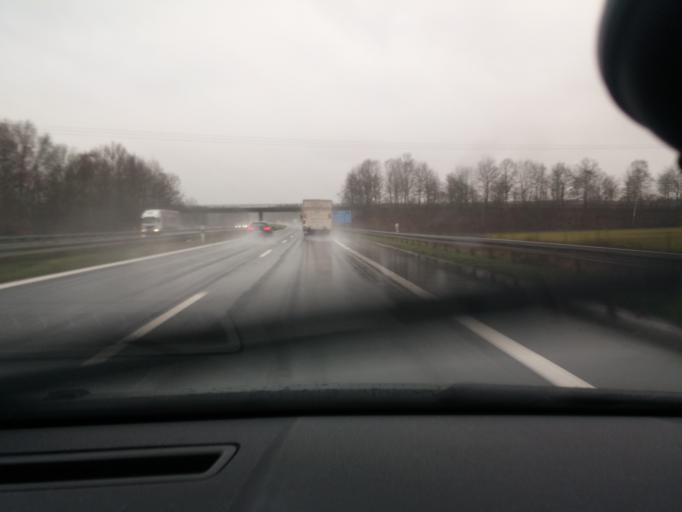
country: DE
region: Bavaria
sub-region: Regierungsbezirk Unterfranken
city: Alzenau in Unterfranken
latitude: 50.0790
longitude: 9.0358
